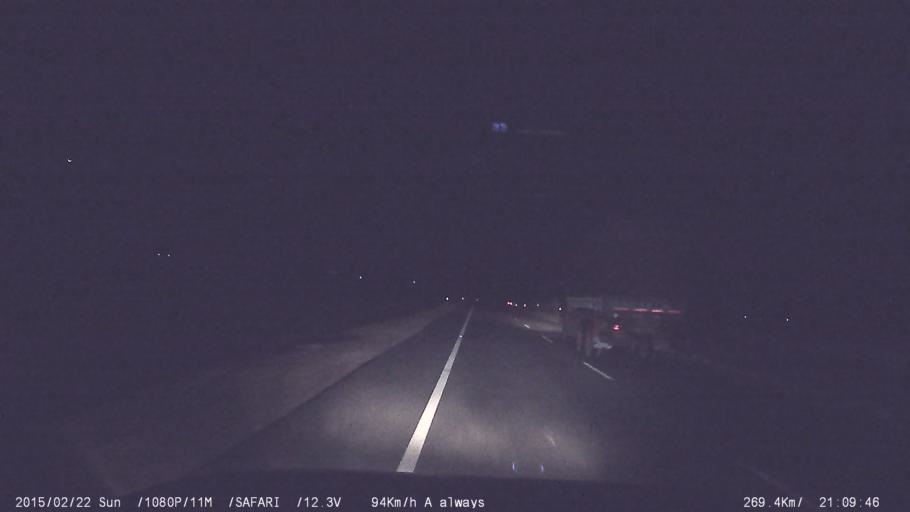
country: IN
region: Tamil Nadu
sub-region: Karur
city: Pallappatti
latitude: 10.7502
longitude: 77.9143
